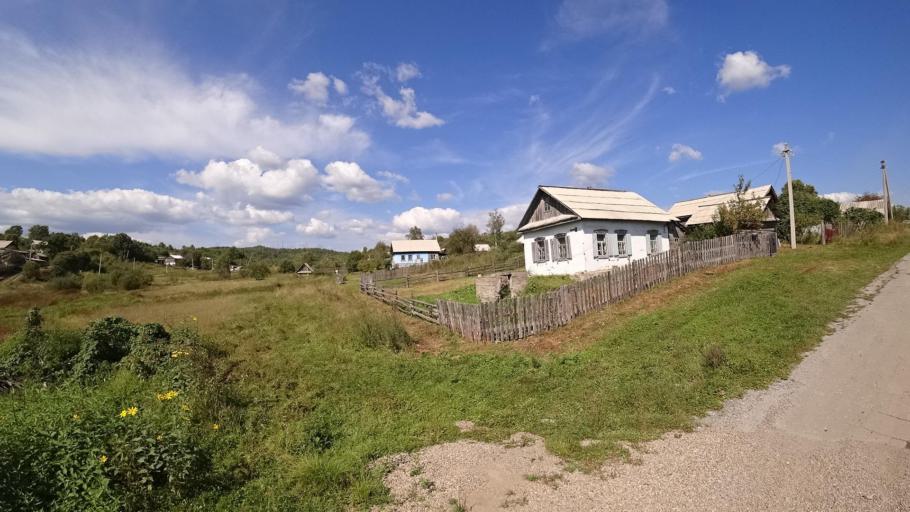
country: RU
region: Jewish Autonomous Oblast
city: Londoko
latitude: 49.0030
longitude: 131.8639
